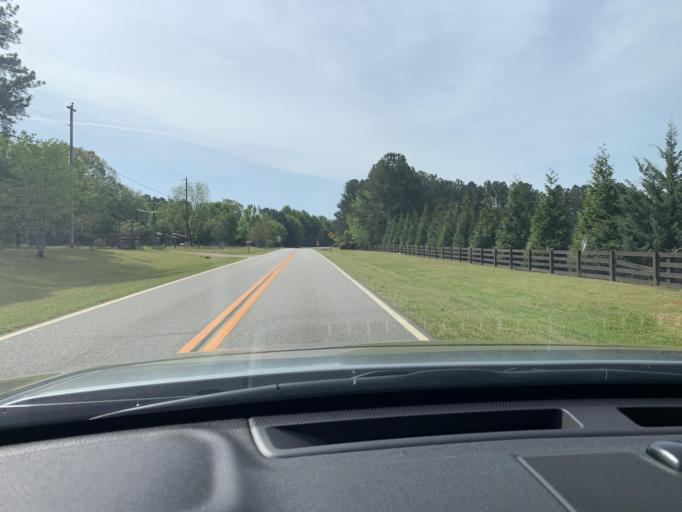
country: US
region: Georgia
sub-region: Oconee County
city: Watkinsville
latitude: 33.8421
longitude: -83.4877
